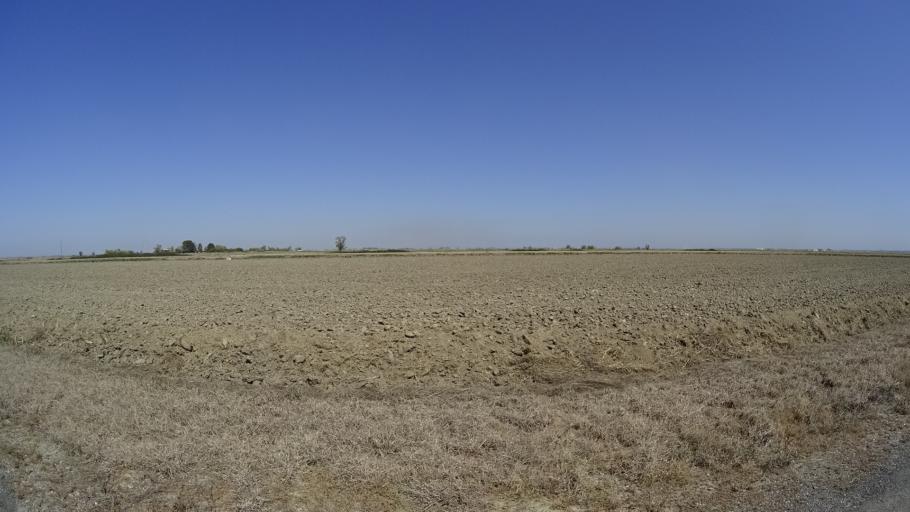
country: US
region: California
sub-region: Glenn County
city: Willows
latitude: 39.4929
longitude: -122.0904
